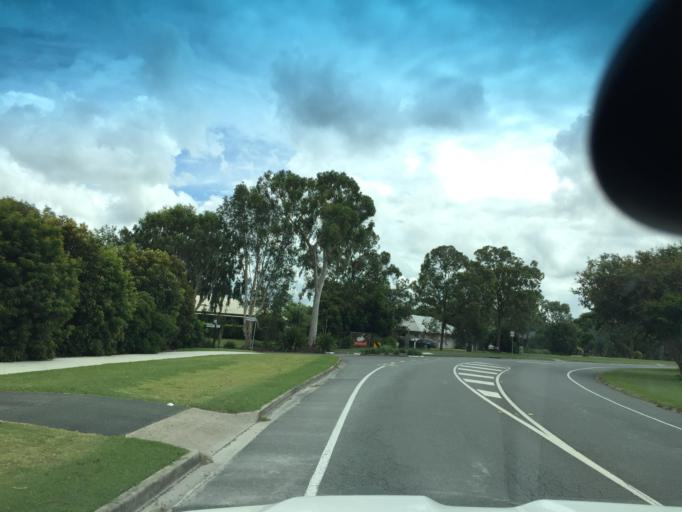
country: AU
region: Queensland
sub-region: Moreton Bay
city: Burpengary
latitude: -27.1329
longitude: 152.9836
